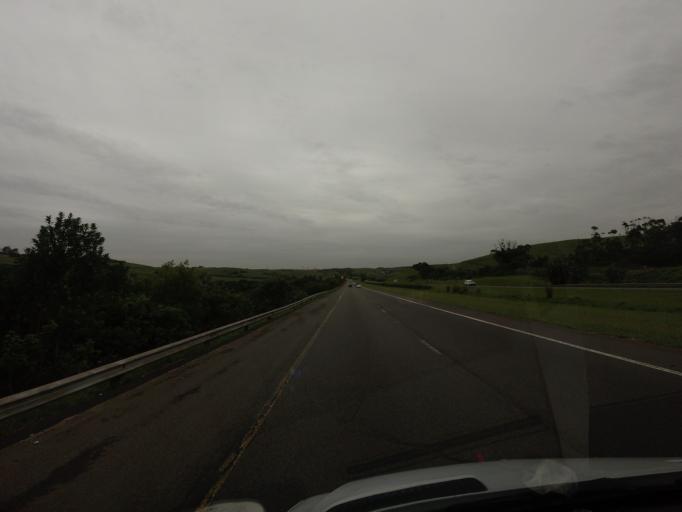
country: ZA
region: KwaZulu-Natal
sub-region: eThekwini Metropolitan Municipality
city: Durban
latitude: -29.6924
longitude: 31.0816
